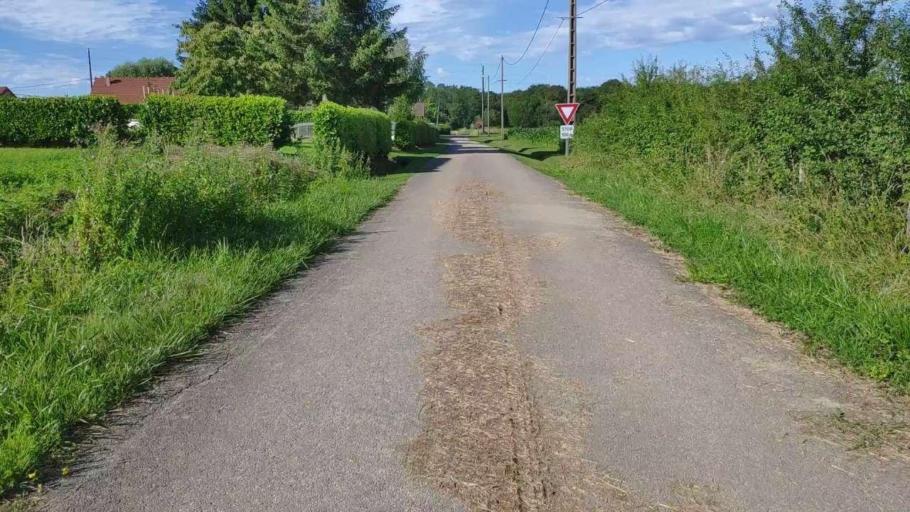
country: FR
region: Franche-Comte
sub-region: Departement du Jura
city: Bletterans
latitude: 46.8260
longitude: 5.4930
